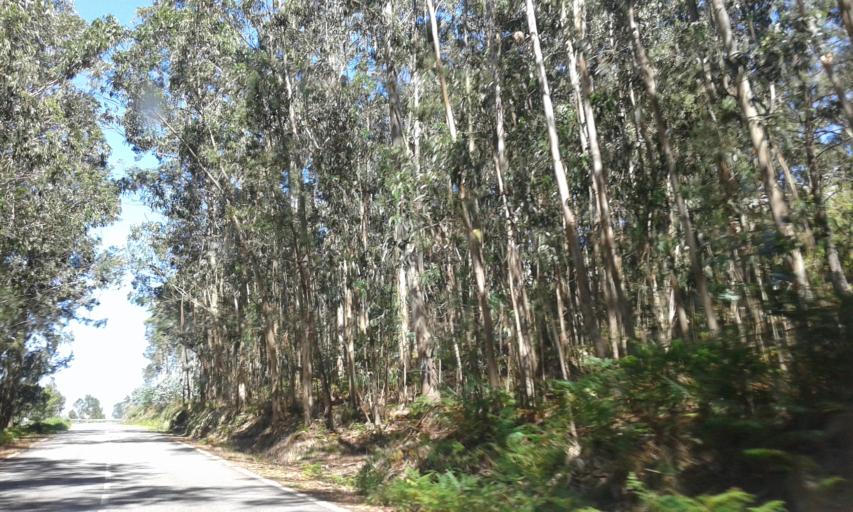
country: ES
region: Galicia
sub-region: Provincia de Pontevedra
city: Baiona
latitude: 42.0997
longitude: -8.8625
